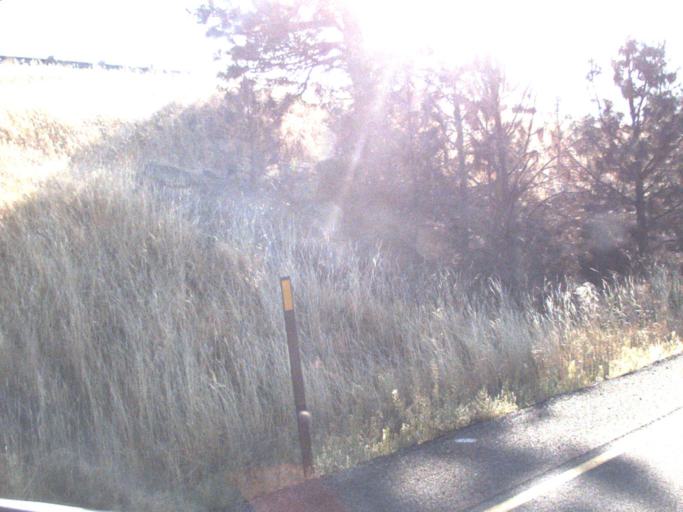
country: US
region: Washington
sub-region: Spokane County
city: Liberty Lake
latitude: 47.7017
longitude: -117.1484
